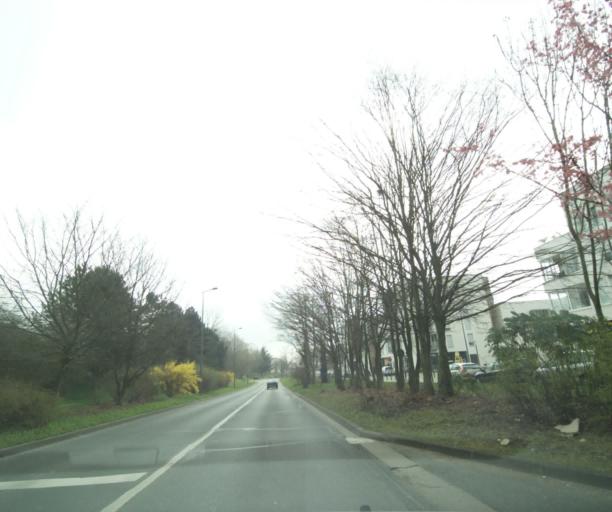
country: FR
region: Ile-de-France
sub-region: Departement du Val-d'Oise
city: Vaureal
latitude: 49.0445
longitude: 2.0271
